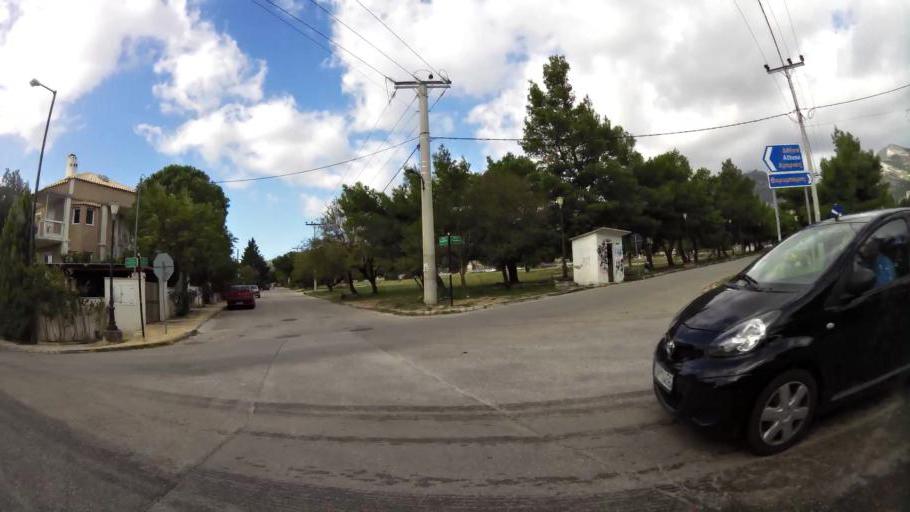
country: GR
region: Attica
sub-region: Nomarchia Anatolikis Attikis
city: Thrakomakedones
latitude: 38.1275
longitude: 23.7586
